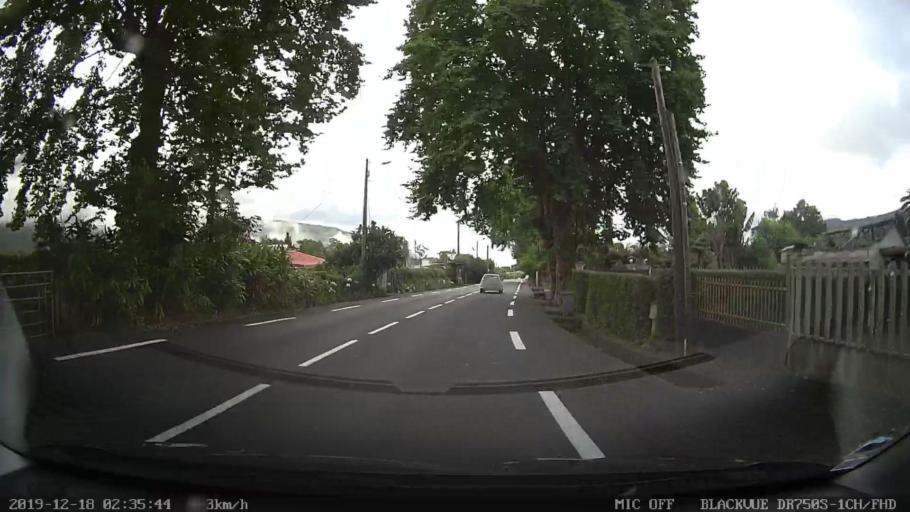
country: RE
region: Reunion
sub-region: Reunion
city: Salazie
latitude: -21.1457
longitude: 55.6182
